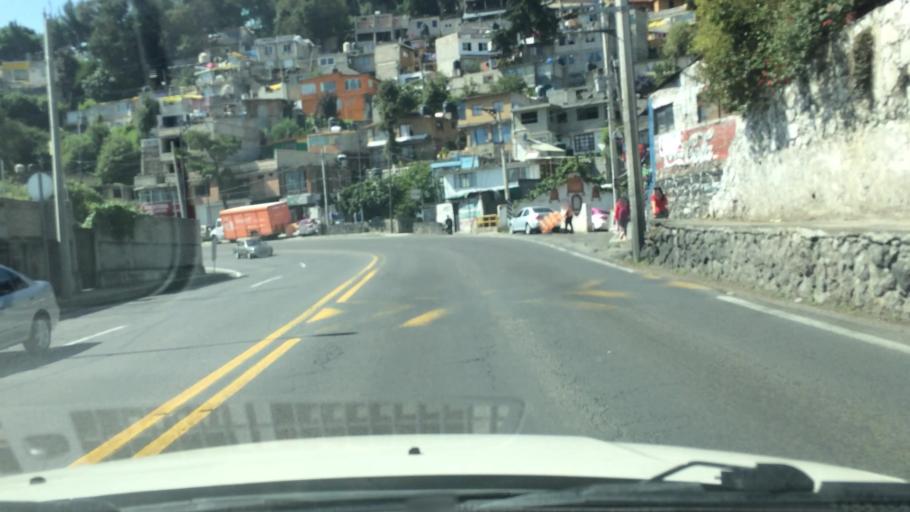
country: MX
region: Mexico City
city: Tlalpan
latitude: 19.2511
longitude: -99.1767
